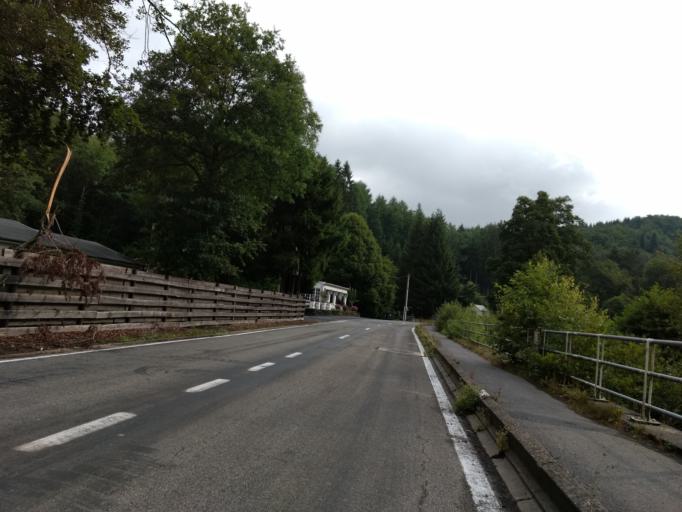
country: BE
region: Wallonia
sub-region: Province du Luxembourg
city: Houffalize
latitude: 50.1310
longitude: 5.7719
